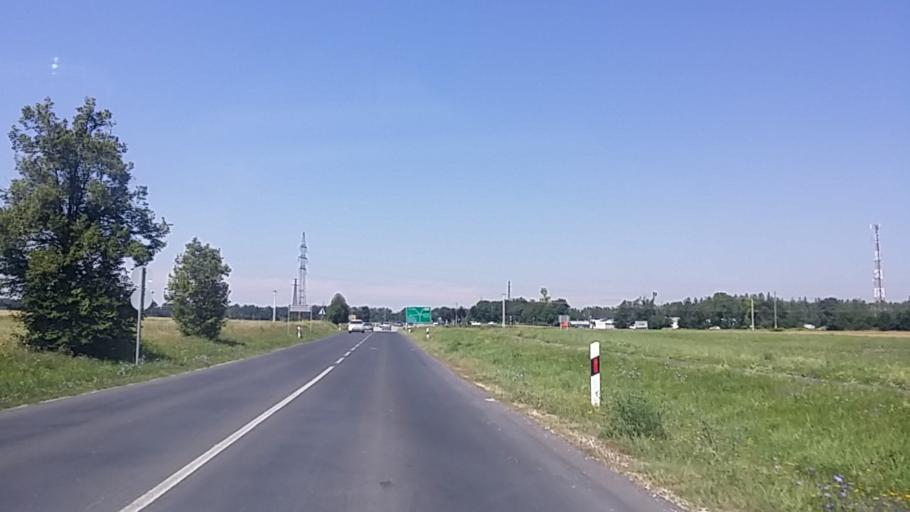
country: HU
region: Zala
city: Keszthely
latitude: 46.7762
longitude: 17.2303
